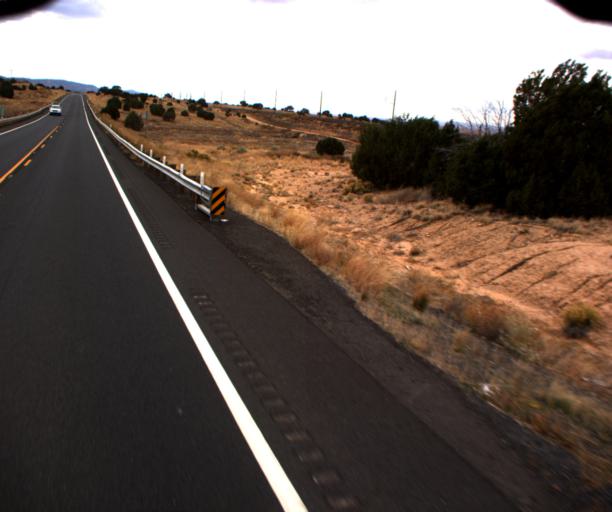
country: US
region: Arizona
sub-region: Navajo County
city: Kayenta
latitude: 36.4957
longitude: -110.6250
